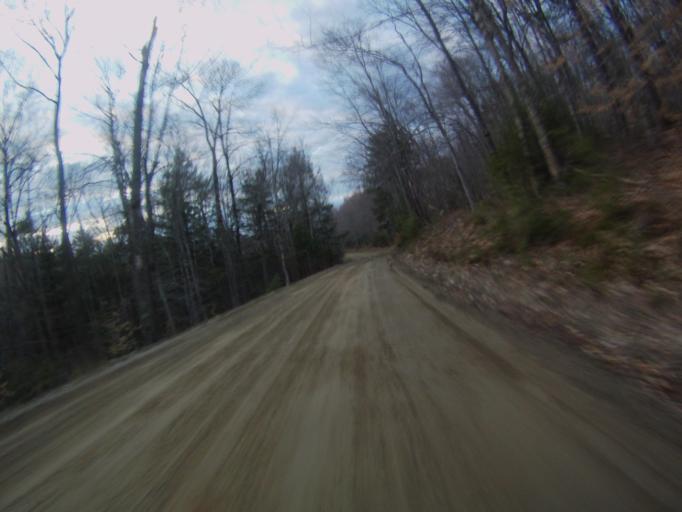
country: US
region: Vermont
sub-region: Rutland County
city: Brandon
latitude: 43.9445
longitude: -73.0240
